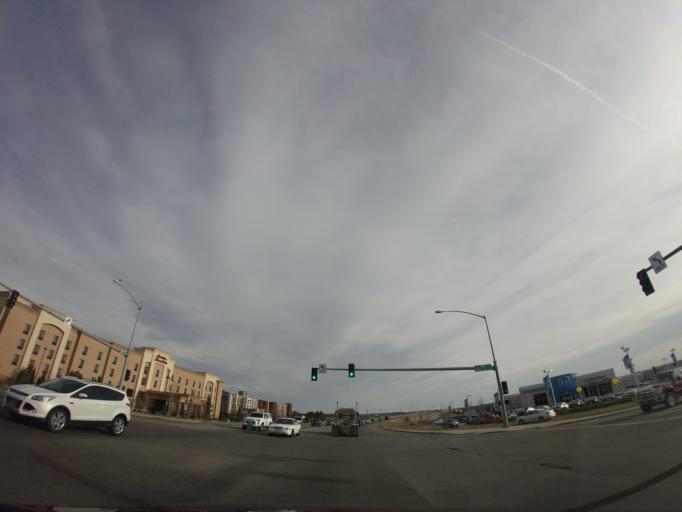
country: US
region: Montana
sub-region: Yellowstone County
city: Billings
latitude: 45.7352
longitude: -108.6088
